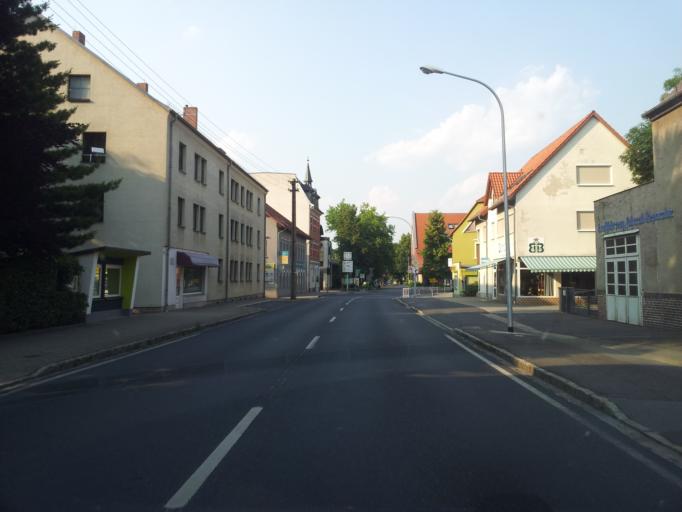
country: DE
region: Saxony
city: Schwepnitz
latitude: 51.3300
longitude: 13.9565
